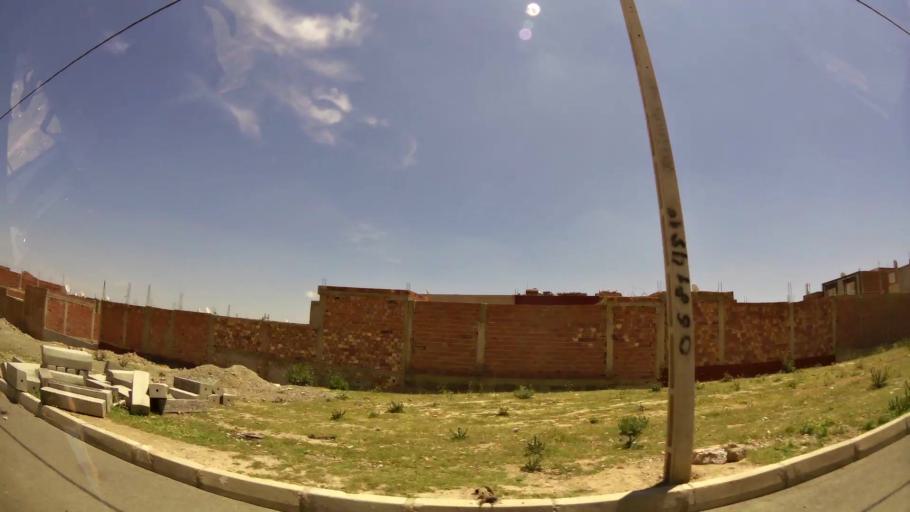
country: MA
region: Oriental
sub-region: Oujda-Angad
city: Oujda
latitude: 34.6543
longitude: -1.9367
